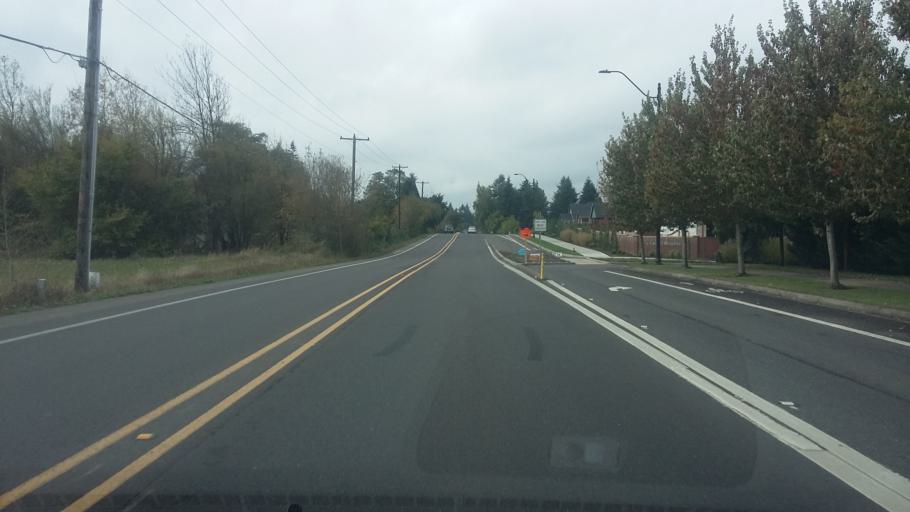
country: US
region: Washington
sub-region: Clark County
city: Ridgefield
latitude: 45.8157
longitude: -122.7071
